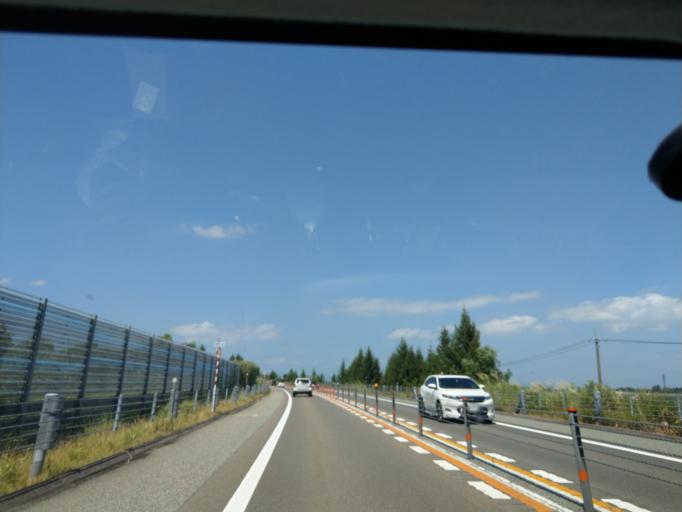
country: JP
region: Akita
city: Omagari
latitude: 39.3935
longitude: 140.4781
